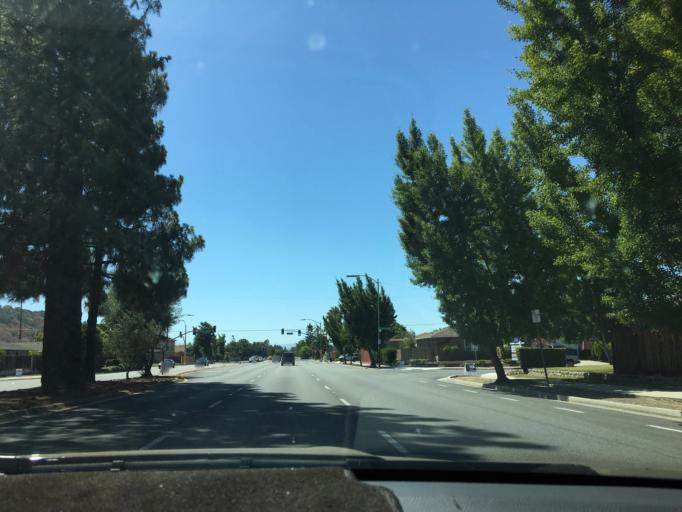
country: US
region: California
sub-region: Santa Clara County
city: Seven Trees
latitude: 37.2385
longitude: -121.8492
